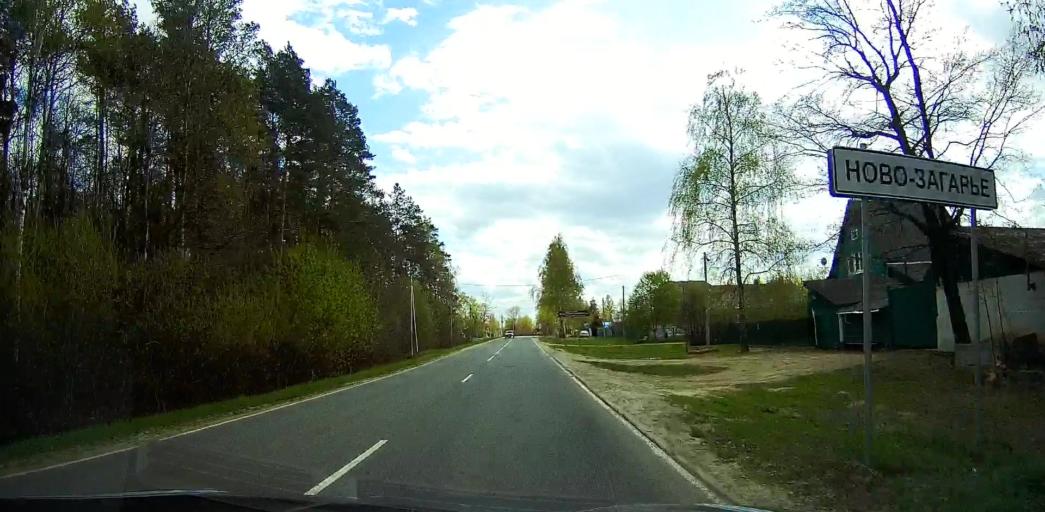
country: RU
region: Moskovskaya
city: Davydovo
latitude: 55.6500
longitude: 38.7550
